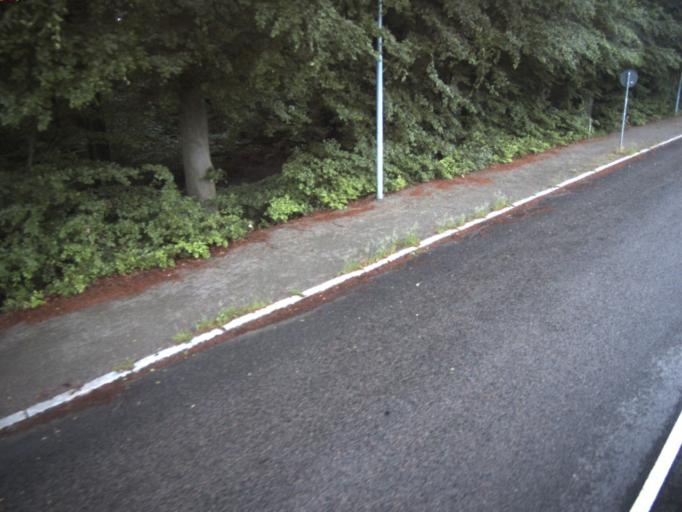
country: SE
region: Skane
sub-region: Helsingborg
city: Helsingborg
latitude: 56.0236
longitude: 12.7491
